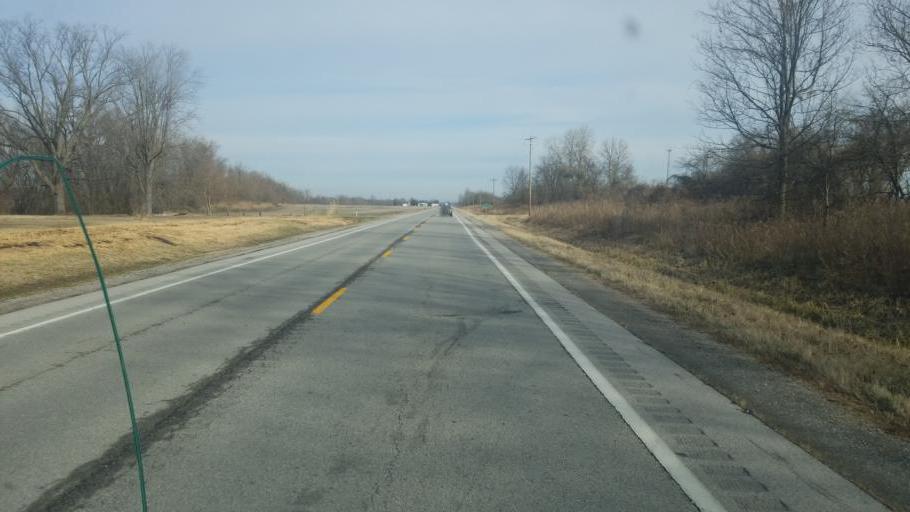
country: US
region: Missouri
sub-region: Cape Girardeau County
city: Cape Girardeau
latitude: 37.3337
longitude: -89.4105
